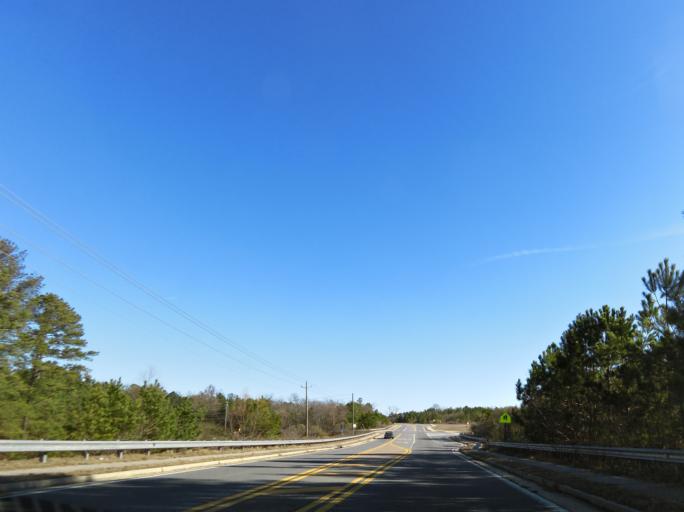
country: US
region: Georgia
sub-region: Peach County
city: Byron
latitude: 32.7370
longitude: -83.7185
